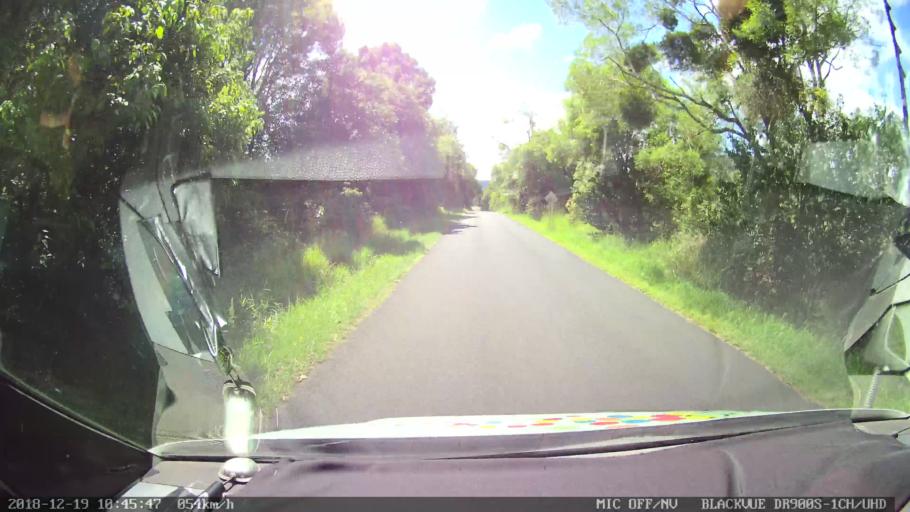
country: AU
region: New South Wales
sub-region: Lismore Municipality
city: Nimbin
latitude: -28.5986
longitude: 153.1925
